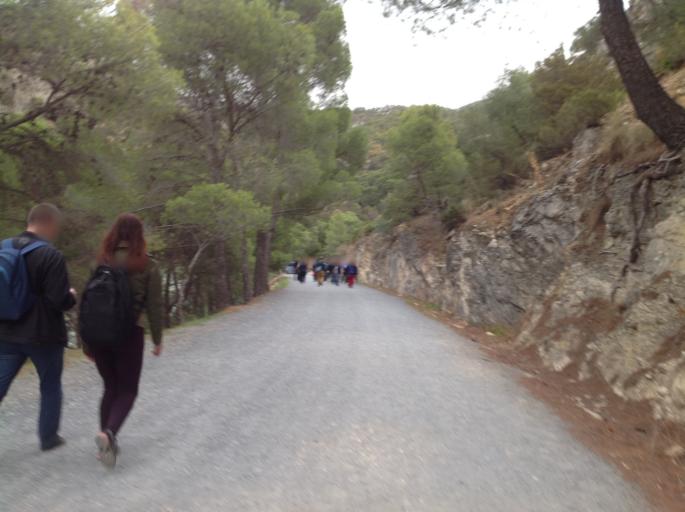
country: ES
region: Andalusia
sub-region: Provincia de Malaga
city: Ardales
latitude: 36.9313
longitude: -4.7906
